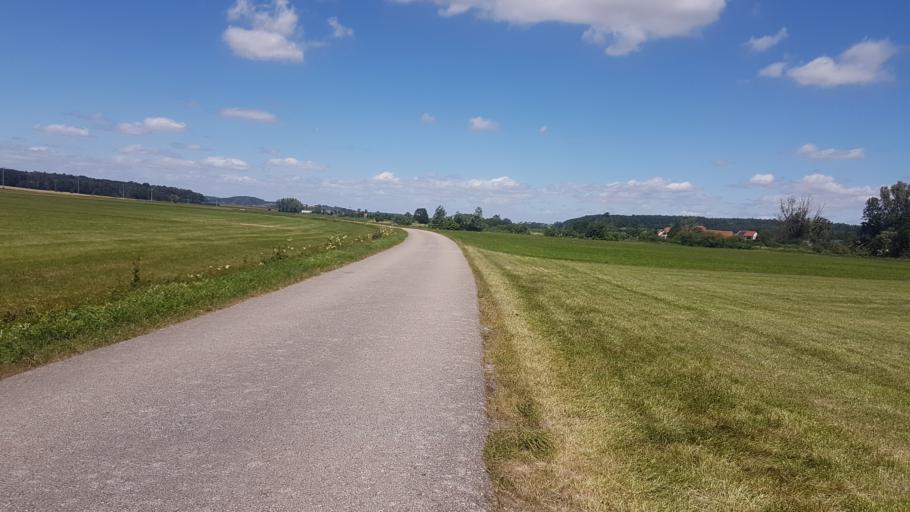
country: DE
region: Bavaria
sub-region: Regierungsbezirk Mittelfranken
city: Aurach
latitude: 49.2698
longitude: 10.4422
